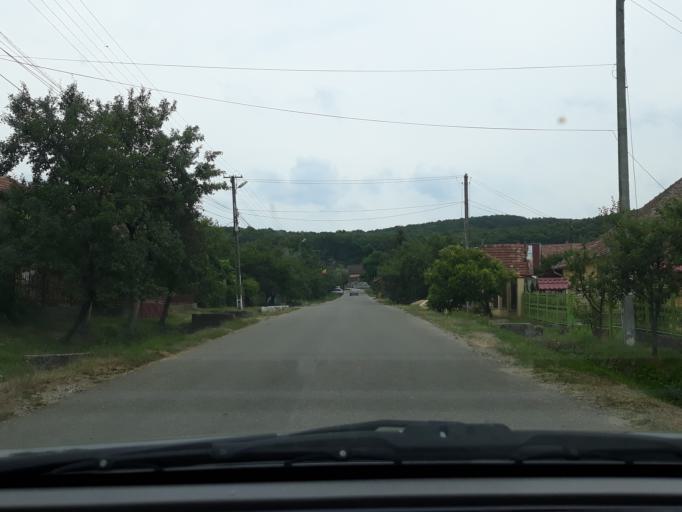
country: RO
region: Salaj
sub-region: Comuna Criseni
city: Criseni
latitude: 47.2514
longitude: 23.0686
